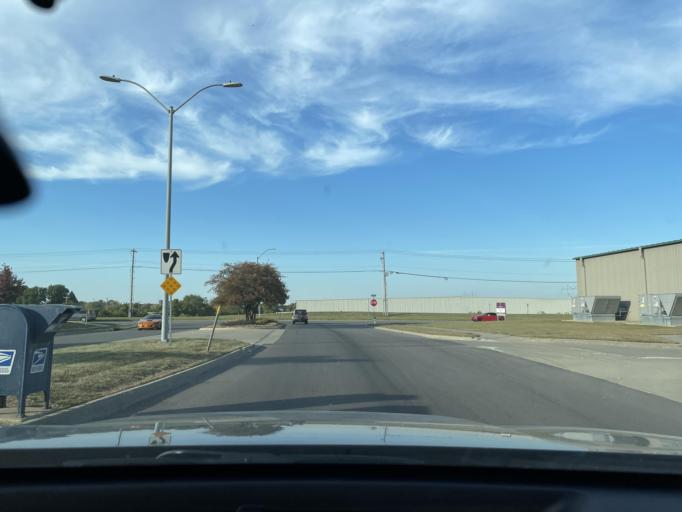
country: US
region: Missouri
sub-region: Buchanan County
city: Saint Joseph
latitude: 39.7547
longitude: -94.7648
